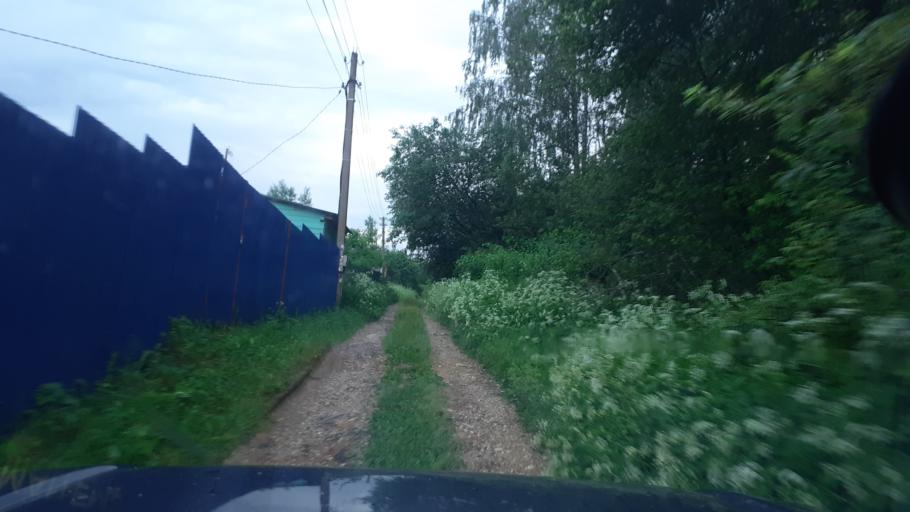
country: RU
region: Moskovskaya
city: Ateptsevo
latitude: 55.3004
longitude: 36.7651
